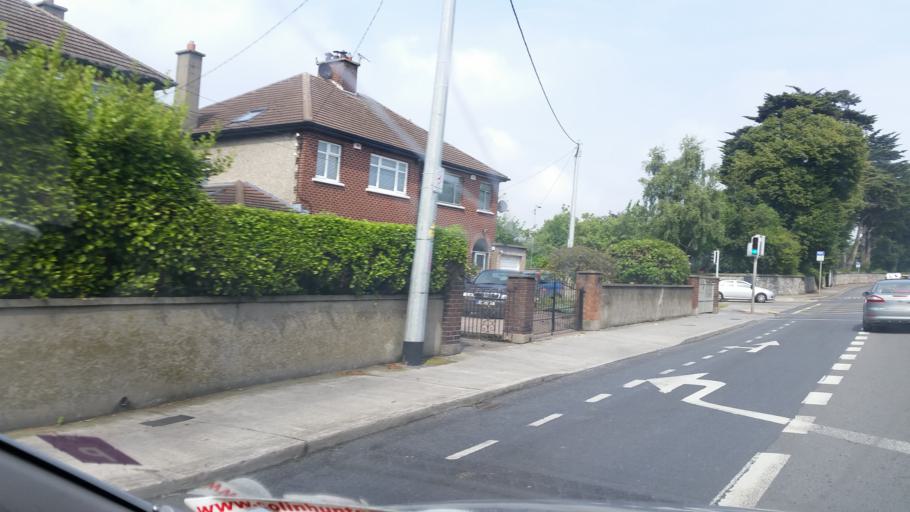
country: IE
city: Donnycarney
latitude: 53.3770
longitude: -6.2160
